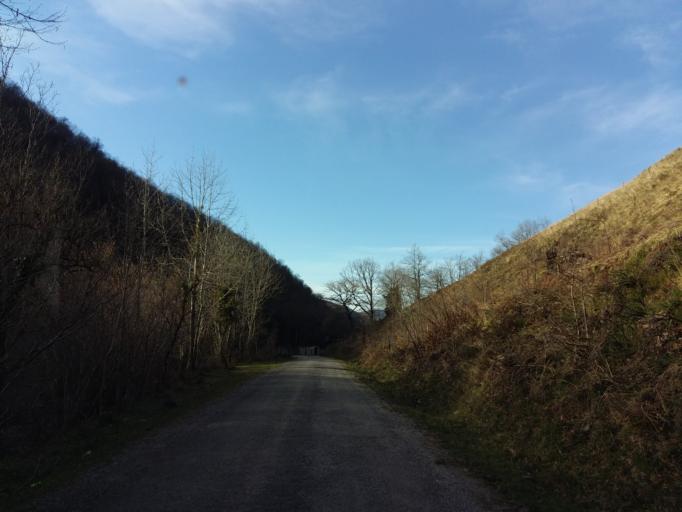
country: ES
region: Cantabria
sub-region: Provincia de Cantabria
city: Vega de Pas
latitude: 43.1322
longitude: -3.7858
